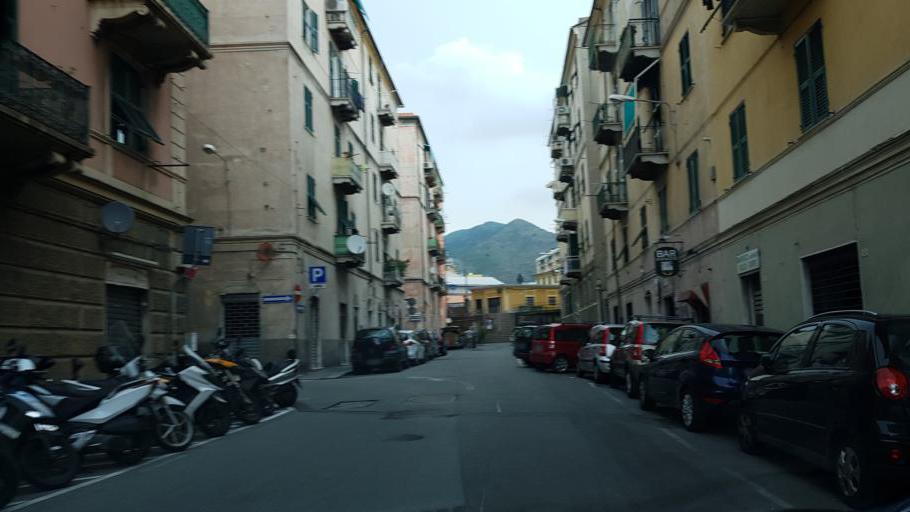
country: IT
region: Liguria
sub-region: Provincia di Genova
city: San Teodoro
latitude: 44.4248
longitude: 8.8530
